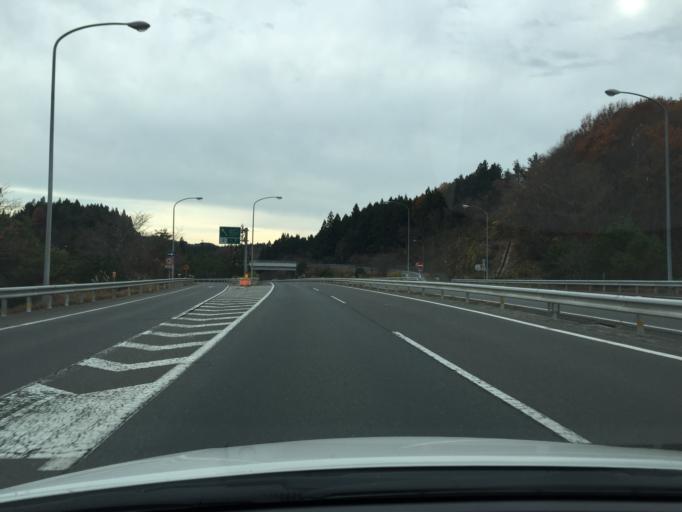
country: JP
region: Fukushima
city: Funehikimachi-funehiki
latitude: 37.2925
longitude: 140.6130
